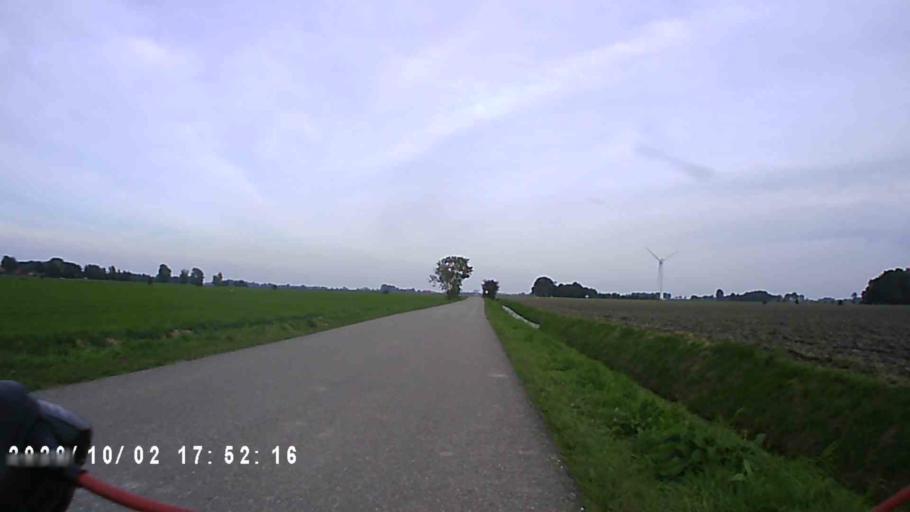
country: NL
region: Groningen
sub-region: Gemeente Zuidhorn
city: Oldehove
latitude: 53.3356
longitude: 6.4205
